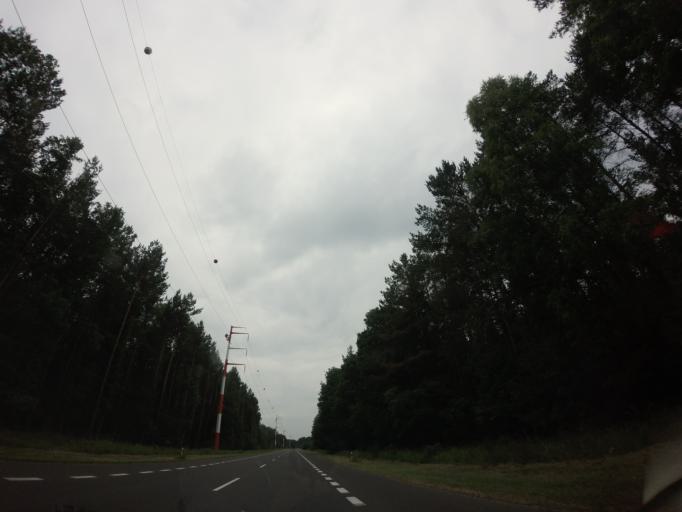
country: PL
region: West Pomeranian Voivodeship
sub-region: Powiat walecki
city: Miroslawiec
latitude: 53.3811
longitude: 16.1478
